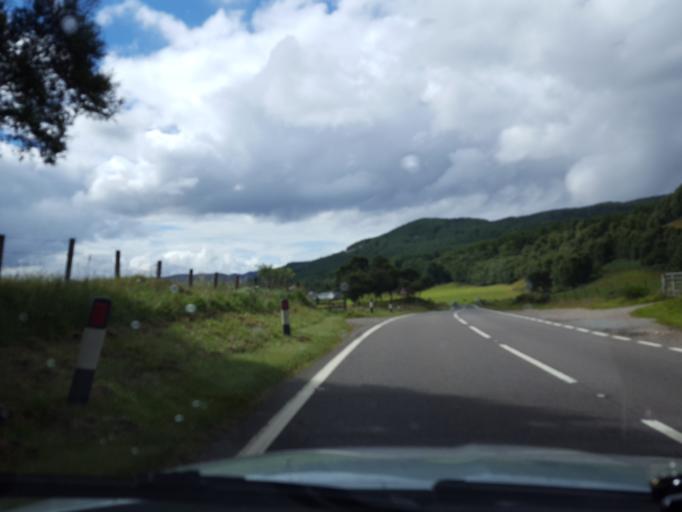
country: GB
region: Scotland
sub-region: Highland
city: Aviemore
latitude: 57.2323
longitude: -3.8092
